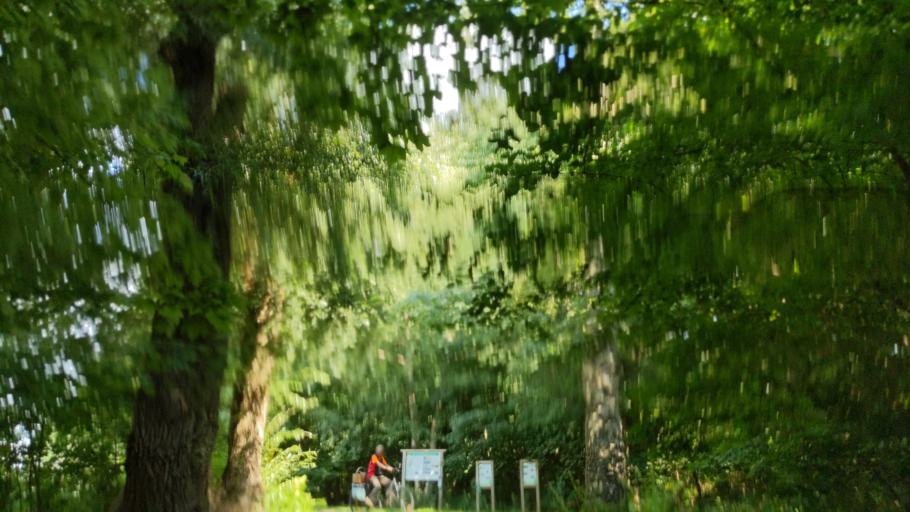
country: DE
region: Schleswig-Holstein
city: Reinfeld
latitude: 53.8420
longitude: 10.4908
